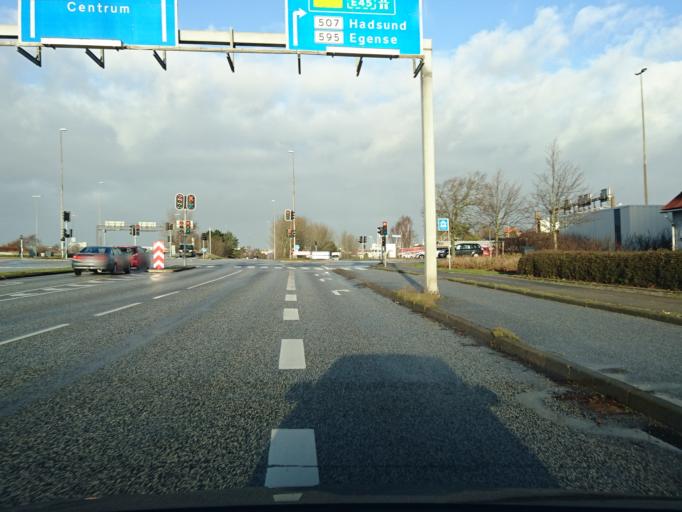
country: DK
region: North Denmark
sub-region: Alborg Kommune
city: Aalborg
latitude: 57.0263
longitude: 9.9274
